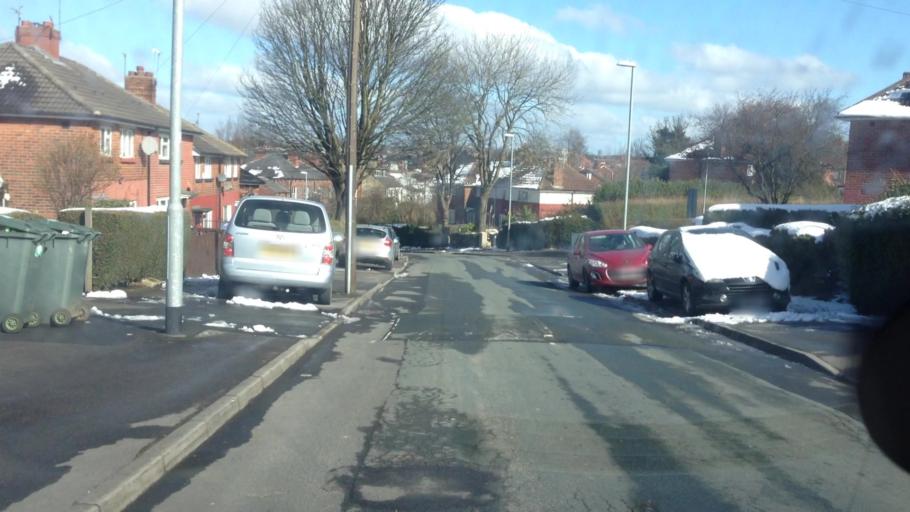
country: GB
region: England
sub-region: City and Borough of Leeds
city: Chapel Allerton
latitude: 53.8272
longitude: -1.5524
